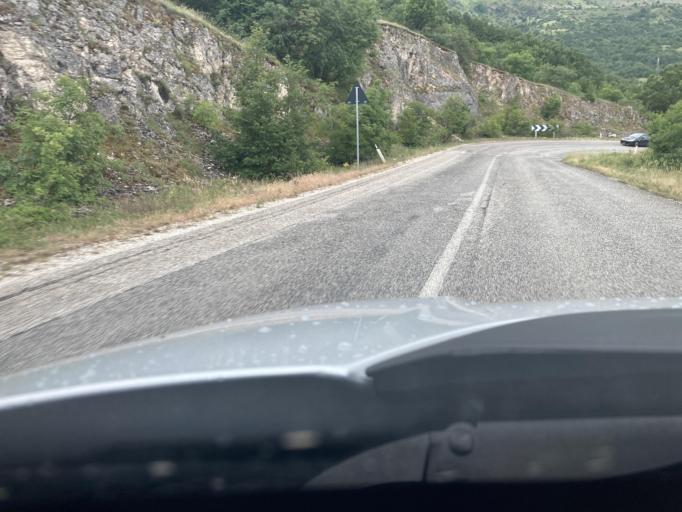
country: IT
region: Abruzzo
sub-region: Provincia dell' Aquila
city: San Panfilo d'Ocre
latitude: 42.2724
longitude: 13.4862
